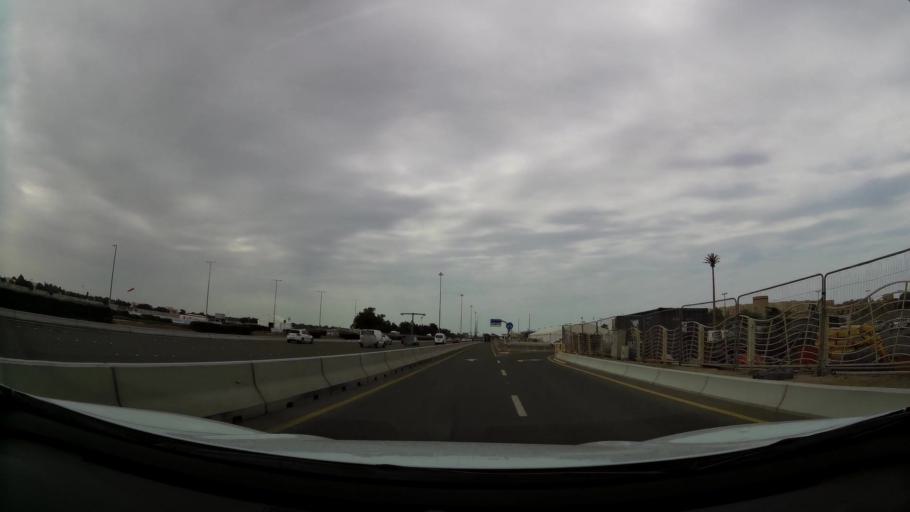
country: AE
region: Abu Dhabi
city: Abu Dhabi
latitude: 24.4178
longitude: 54.4343
